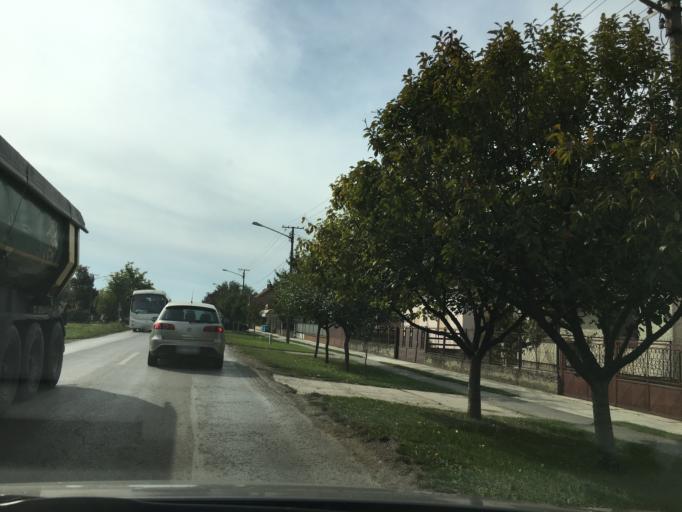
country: RS
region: Autonomna Pokrajina Vojvodina
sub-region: Juznobacki Okrug
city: Temerin
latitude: 45.4325
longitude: 19.8978
